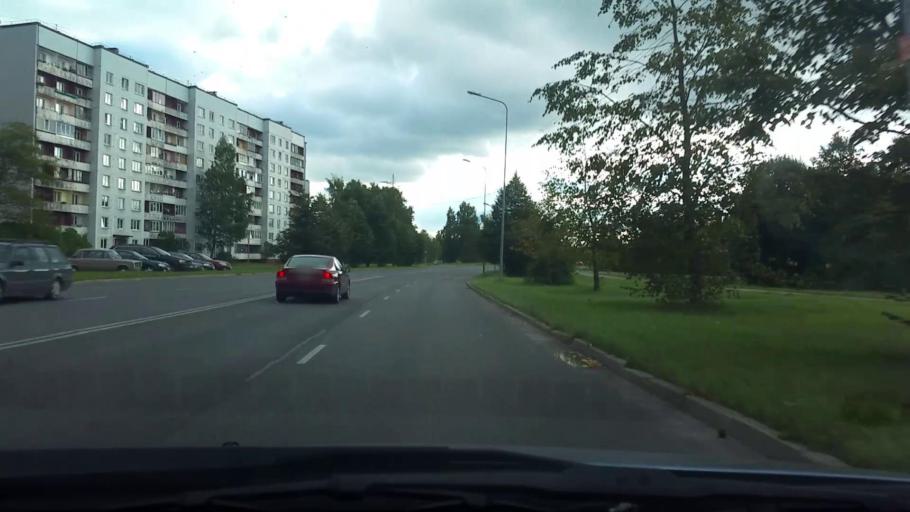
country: LV
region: Stopini
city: Ulbroka
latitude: 56.9627
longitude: 24.2331
